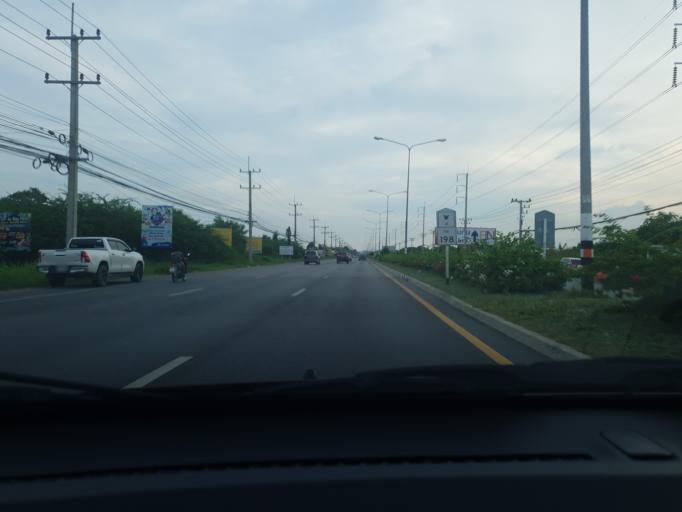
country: TH
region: Phetchaburi
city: Cha-am
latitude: 12.7433
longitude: 99.9596
